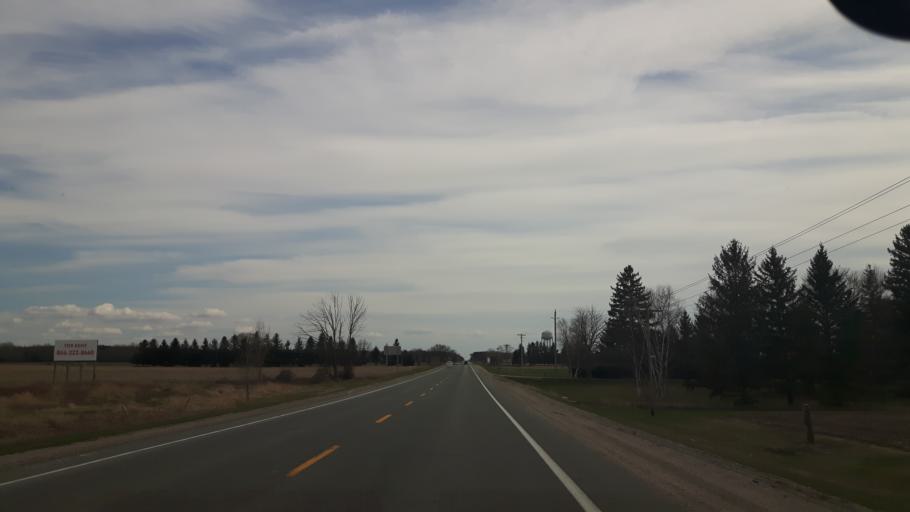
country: CA
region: Ontario
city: Goderich
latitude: 43.6975
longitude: -81.7057
